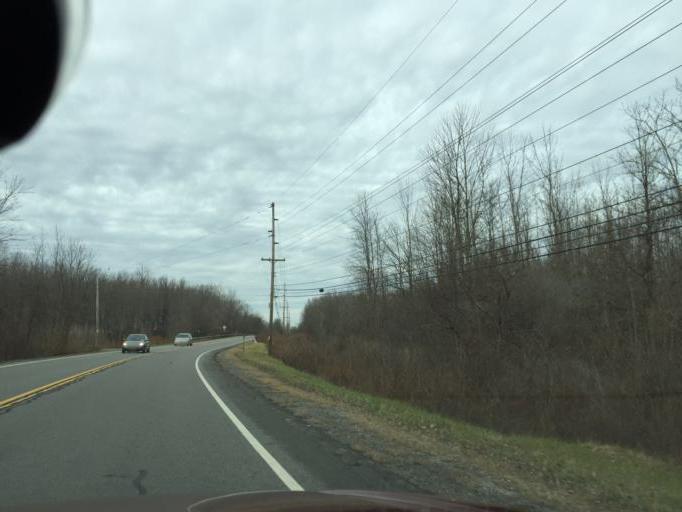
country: US
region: New York
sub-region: Monroe County
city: Scottsville
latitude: 43.0898
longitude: -77.7281
